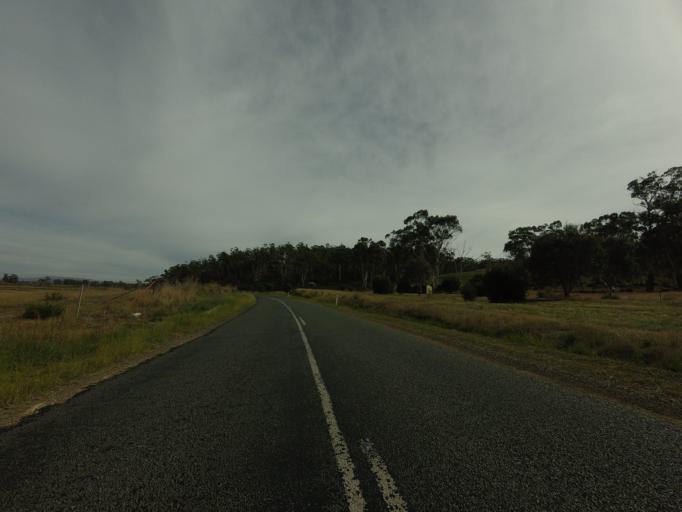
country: AU
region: Tasmania
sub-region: Brighton
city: Bridgewater
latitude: -42.3343
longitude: 147.4008
